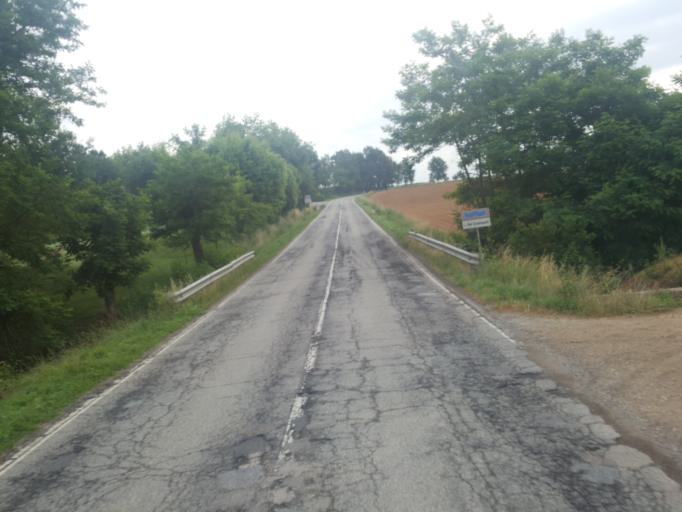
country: IT
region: Piedmont
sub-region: Provincia di Cuneo
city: Ceresole Alba
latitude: 44.8555
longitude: 7.8170
